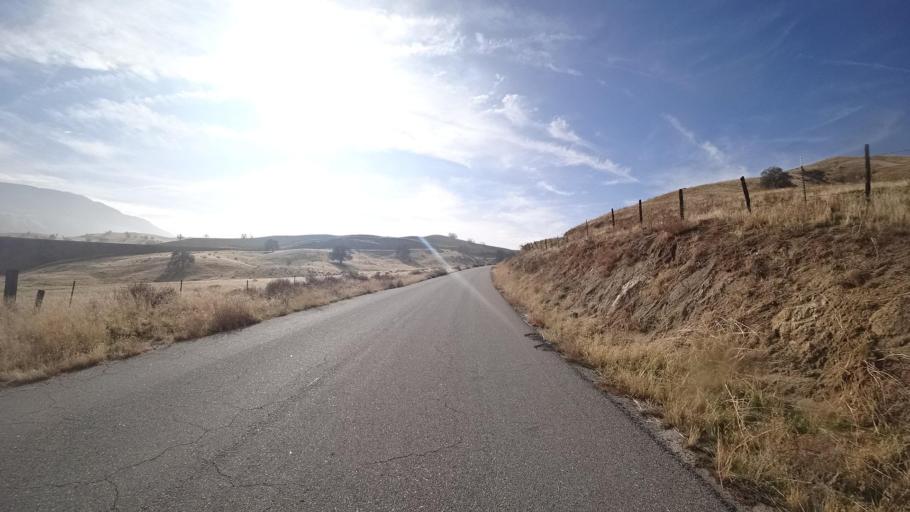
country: US
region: California
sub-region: Kern County
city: Bear Valley Springs
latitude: 35.2886
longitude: -118.6479
